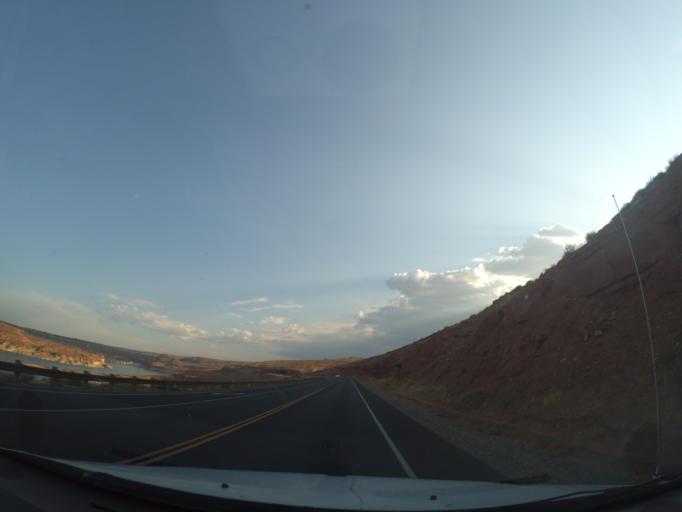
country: US
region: Arizona
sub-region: Coconino County
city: Page
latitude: 36.9626
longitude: -111.4925
